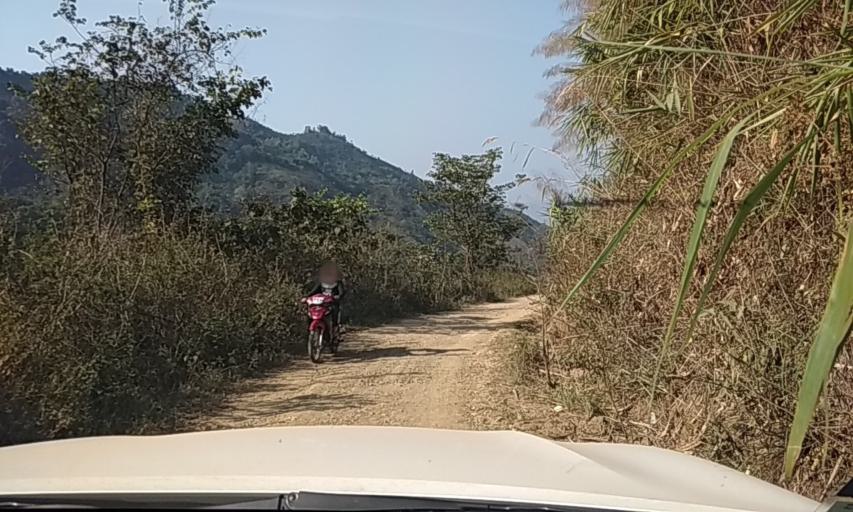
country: LA
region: Phongsali
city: Phongsali
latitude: 21.6911
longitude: 102.1007
